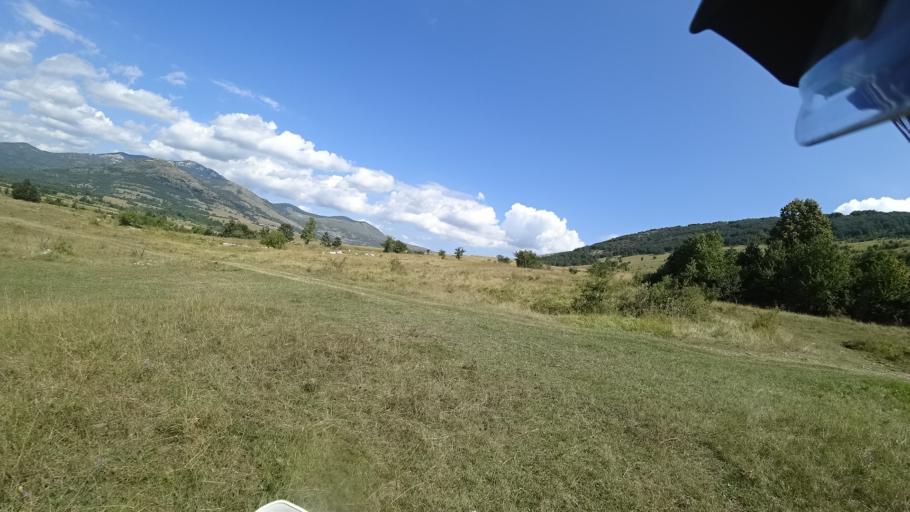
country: HR
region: Zadarska
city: Gracac
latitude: 44.4154
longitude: 15.9273
